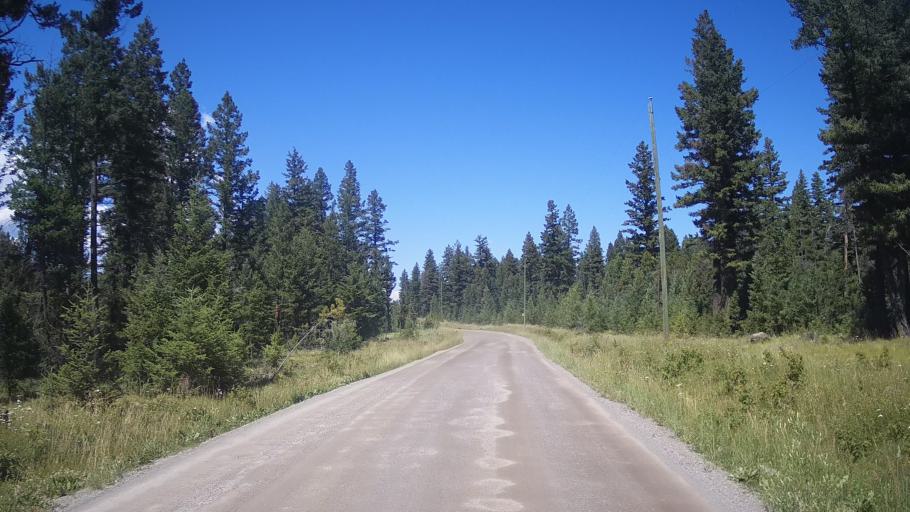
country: CA
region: British Columbia
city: Cache Creek
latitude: 51.2102
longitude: -121.5998
